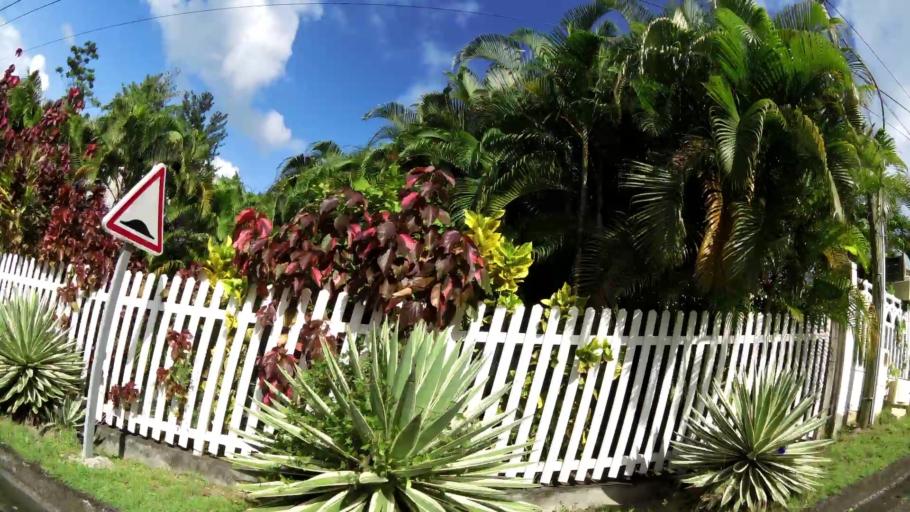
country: MQ
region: Martinique
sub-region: Martinique
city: Ducos
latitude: 14.5756
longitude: -60.9826
